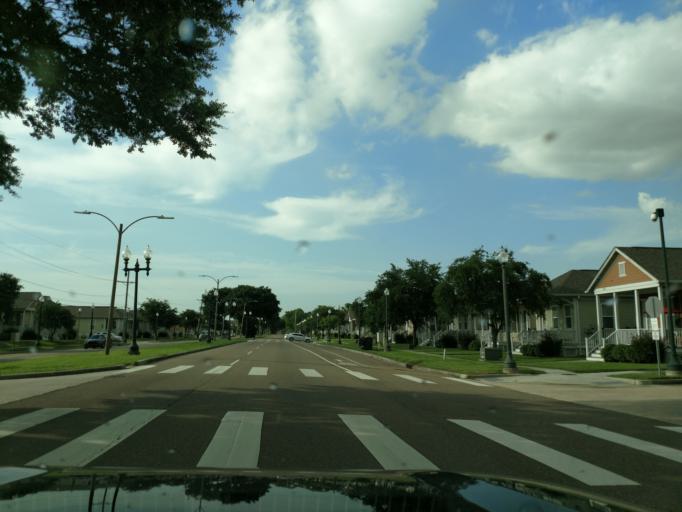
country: US
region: Louisiana
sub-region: Jefferson Parish
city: Gretna
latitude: 29.9313
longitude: -90.0417
